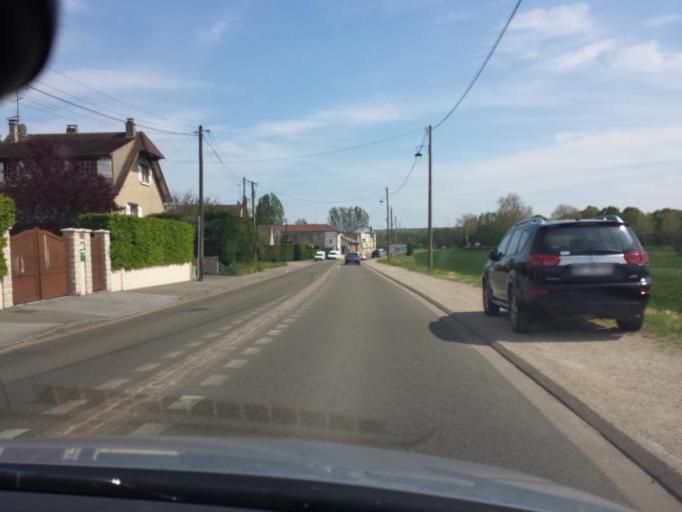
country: FR
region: Ile-de-France
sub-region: Departement des Yvelines
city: Villiers-Saint-Frederic
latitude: 48.8115
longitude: 1.8782
